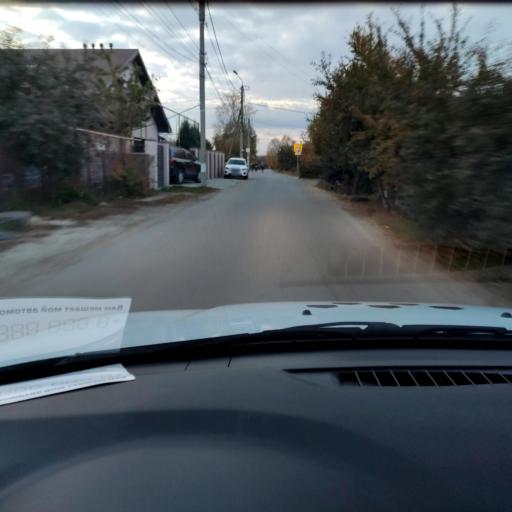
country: RU
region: Samara
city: Tol'yatti
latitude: 53.5363
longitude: 49.4028
